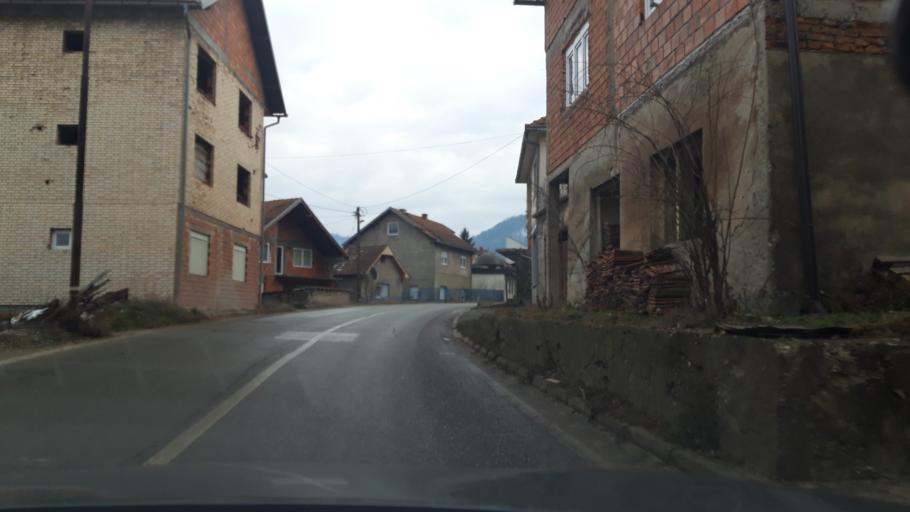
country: RS
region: Central Serbia
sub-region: Macvanski Okrug
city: Mali Zvornik
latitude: 44.3632
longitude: 19.1123
